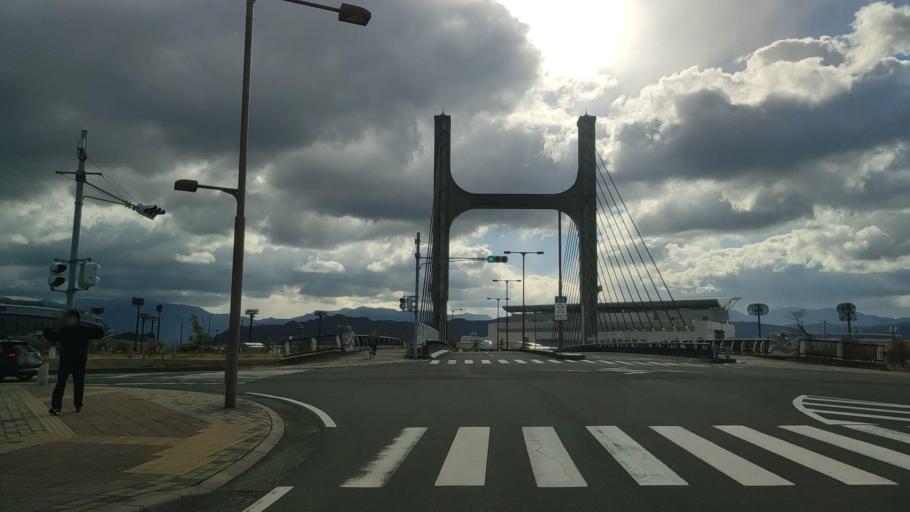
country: JP
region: Ehime
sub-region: Shikoku-chuo Shi
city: Matsuyama
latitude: 33.8113
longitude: 132.7415
